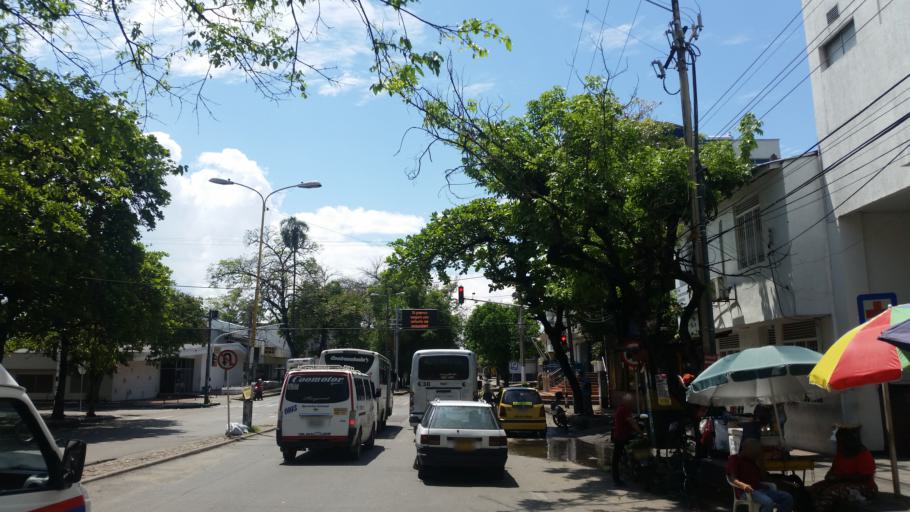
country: CO
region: Huila
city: Neiva
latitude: 2.9308
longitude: -75.2877
